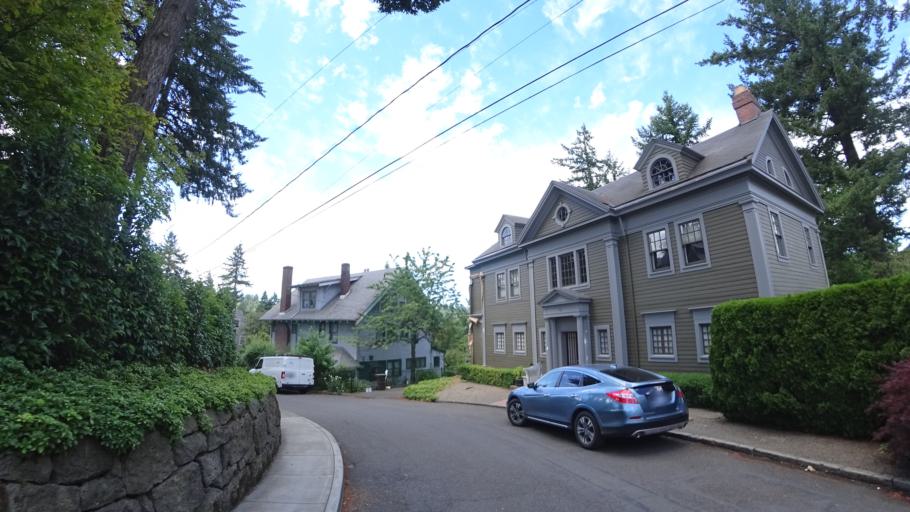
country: US
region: Oregon
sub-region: Multnomah County
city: Portland
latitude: 45.5096
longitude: -122.7049
